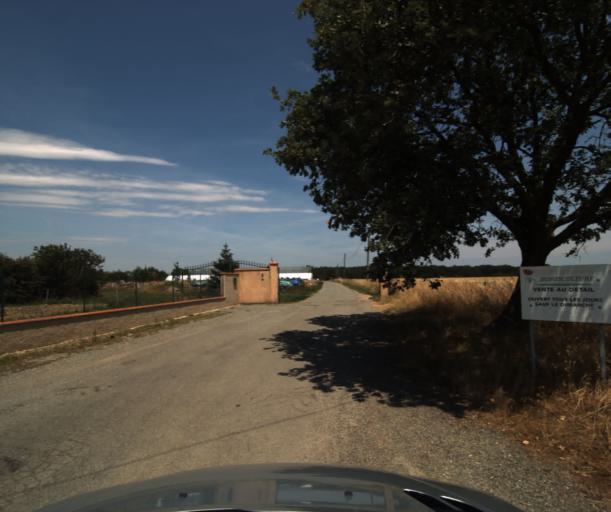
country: FR
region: Midi-Pyrenees
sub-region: Departement de la Haute-Garonne
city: Labastidette
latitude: 43.4620
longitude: 1.2636
